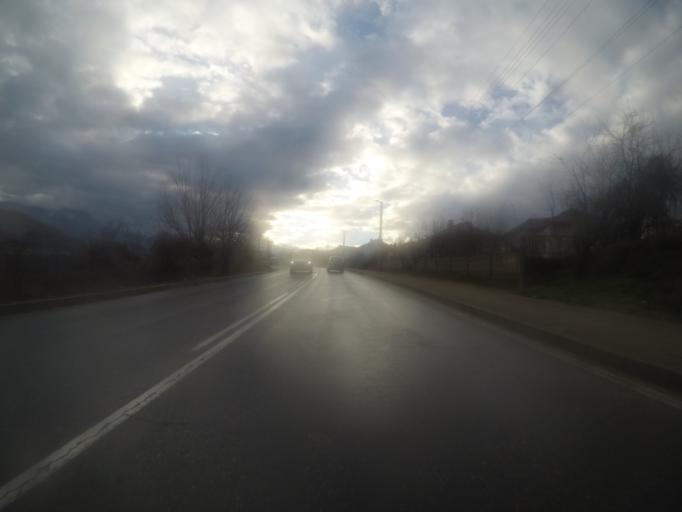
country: BG
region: Blagoevgrad
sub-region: Obshtina Simitli
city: Simitli
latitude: 41.8852
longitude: 23.1196
